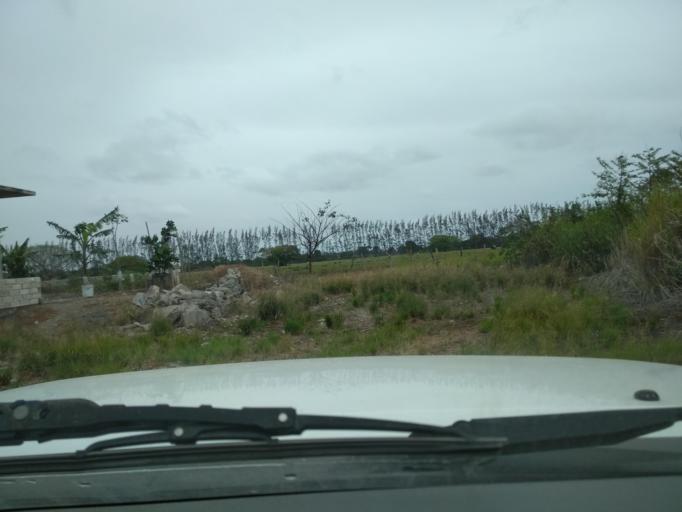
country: MX
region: Veracruz
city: Paso del Toro
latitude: 19.0466
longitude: -96.1317
